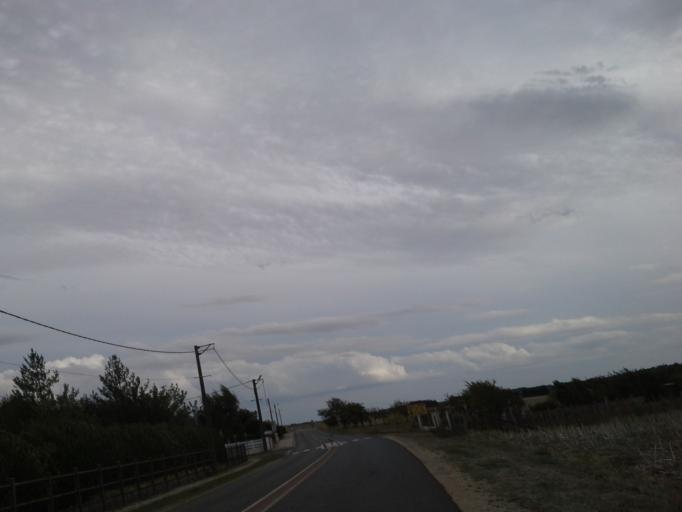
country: FR
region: Centre
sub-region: Departement du Loir-et-Cher
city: Villiers-sur-Loir
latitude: 47.8026
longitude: 0.9962
